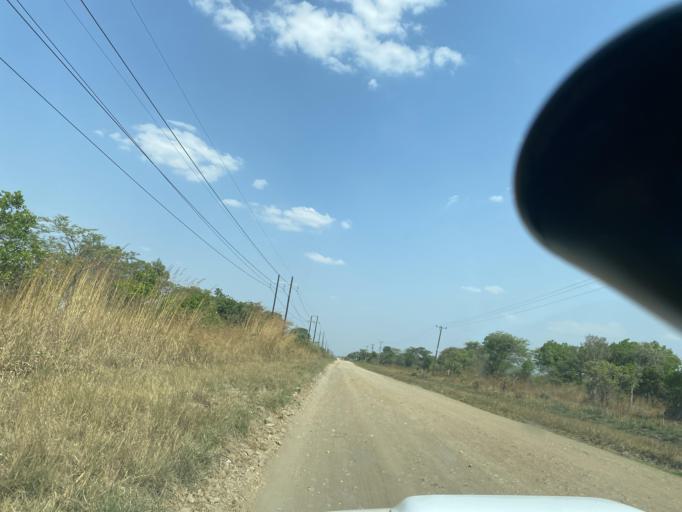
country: ZM
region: Lusaka
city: Lusaka
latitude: -15.3060
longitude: 28.0391
